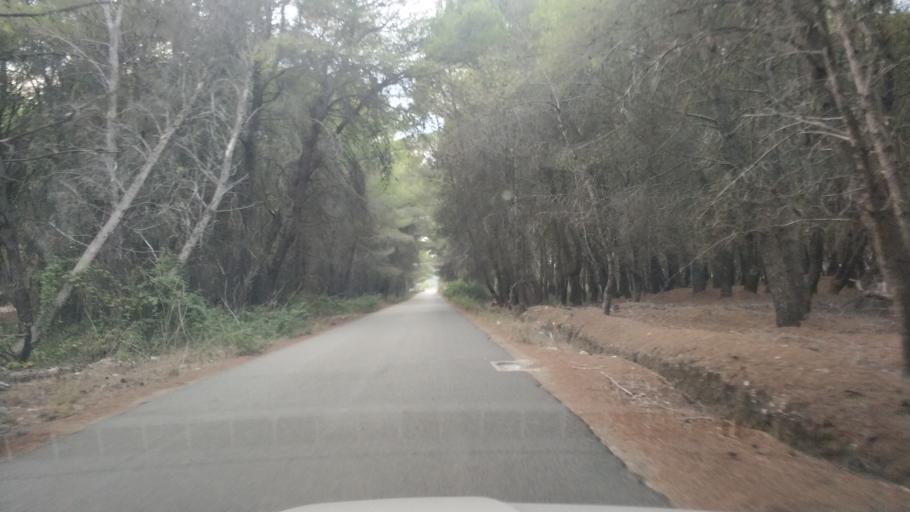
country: AL
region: Vlore
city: Vlore
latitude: 40.4992
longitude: 19.4301
